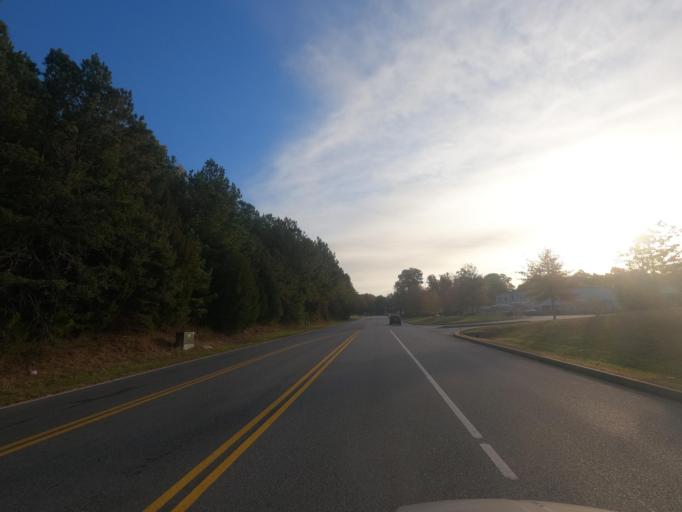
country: US
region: Maryland
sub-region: Calvert County
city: Lusby
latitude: 38.3887
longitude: -76.4344
